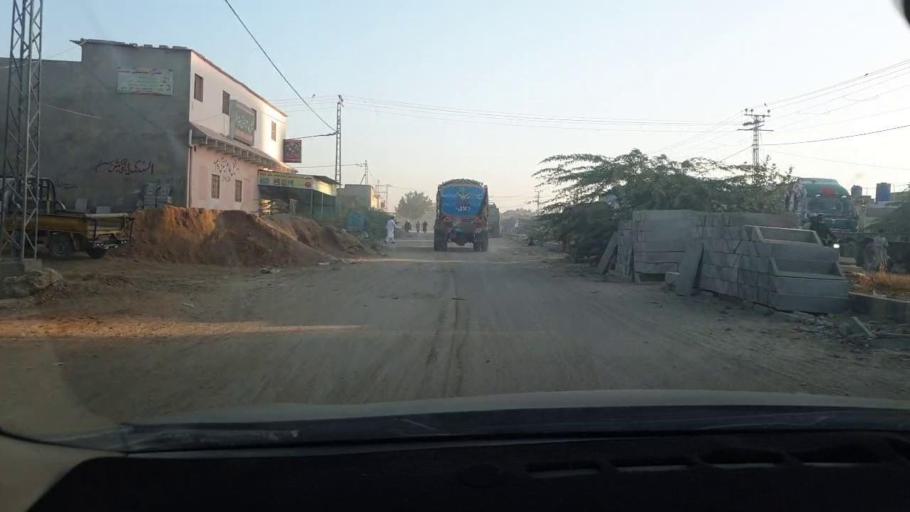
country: PK
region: Sindh
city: Malir Cantonment
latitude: 25.0133
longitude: 67.1690
